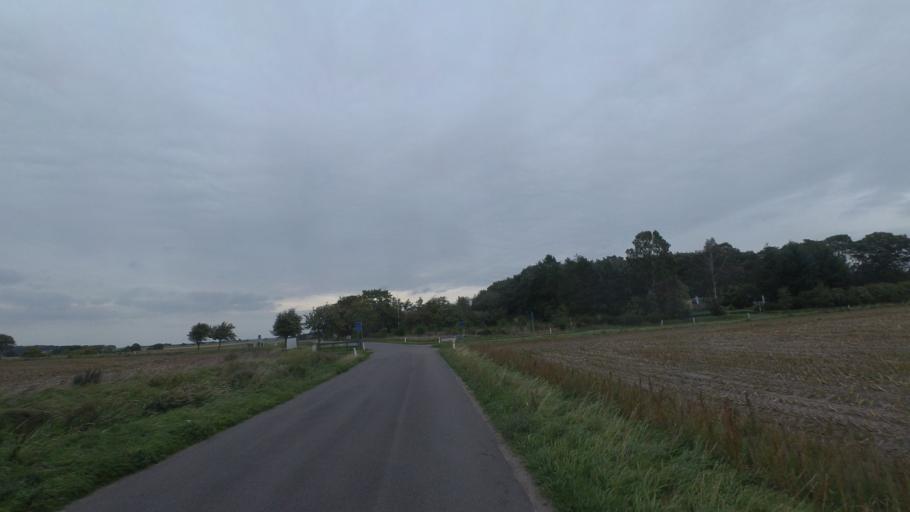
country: DK
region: Capital Region
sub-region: Bornholm Kommune
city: Akirkeby
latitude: 55.0087
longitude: 14.9920
